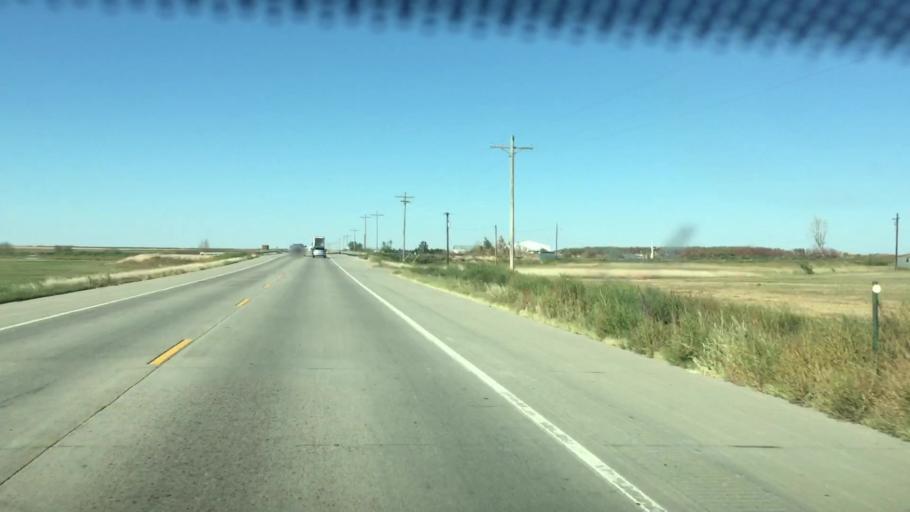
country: US
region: Colorado
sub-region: Prowers County
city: Lamar
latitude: 38.2270
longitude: -102.7240
